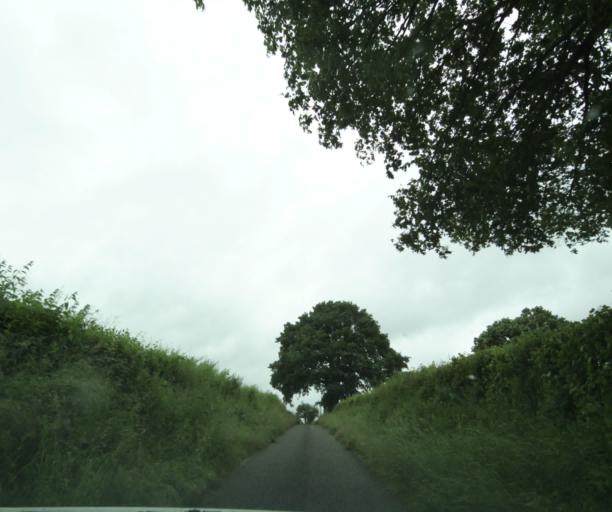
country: FR
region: Bourgogne
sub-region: Departement de Saone-et-Loire
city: Palinges
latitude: 46.5060
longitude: 4.2545
